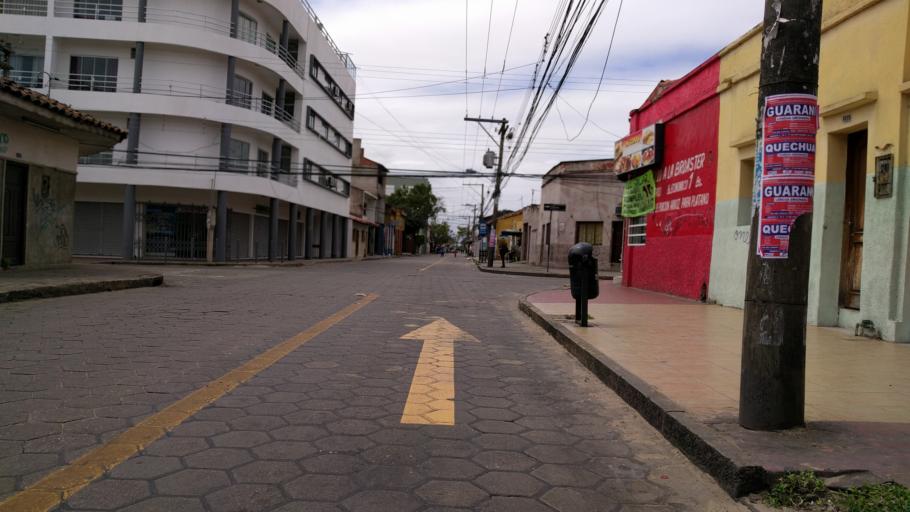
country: BO
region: Santa Cruz
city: Santa Cruz de la Sierra
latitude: -17.7814
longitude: -63.1767
